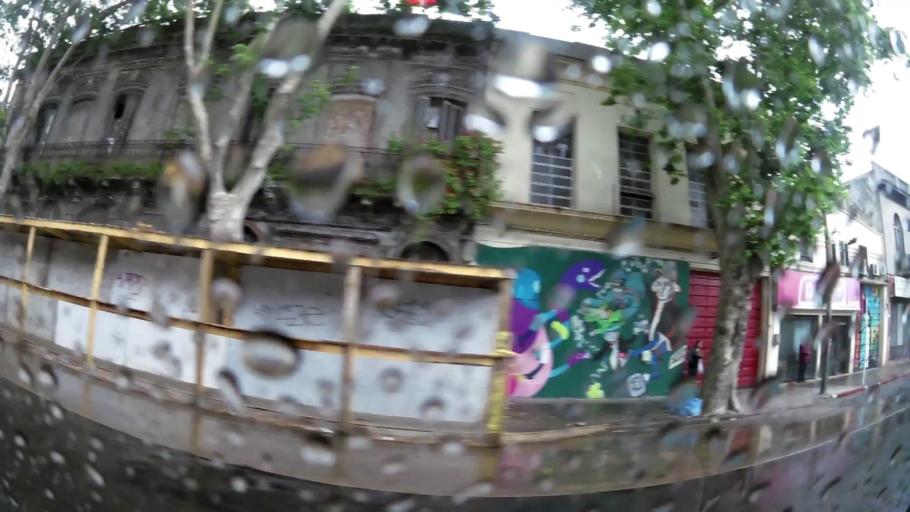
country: UY
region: Montevideo
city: Montevideo
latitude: -34.8874
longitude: -56.1855
